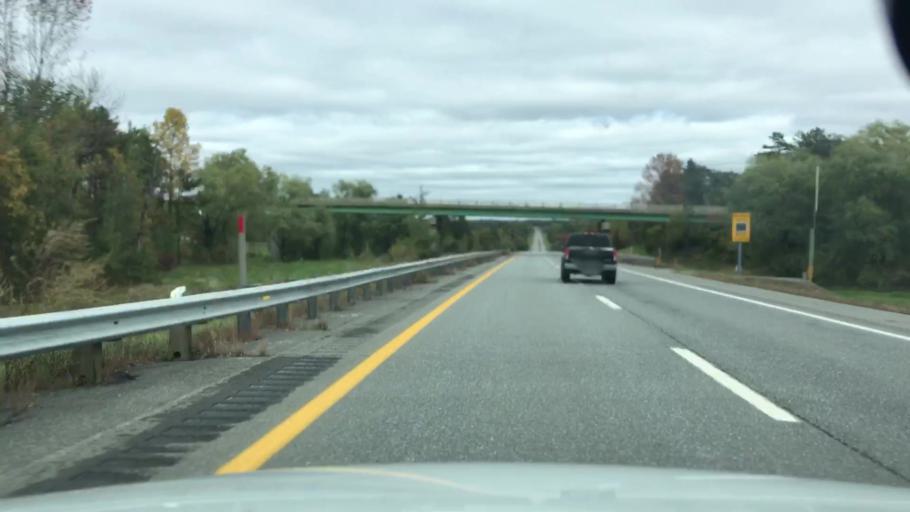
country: US
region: Maine
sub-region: Kennebec County
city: Clinton
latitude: 44.6492
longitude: -69.5165
